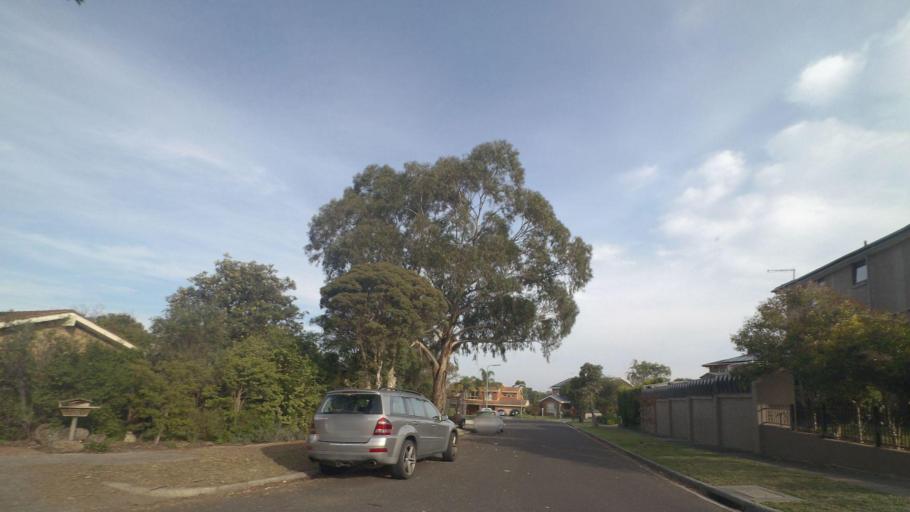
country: AU
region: Victoria
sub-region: Manningham
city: Doncaster East
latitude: -37.7753
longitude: 145.1572
